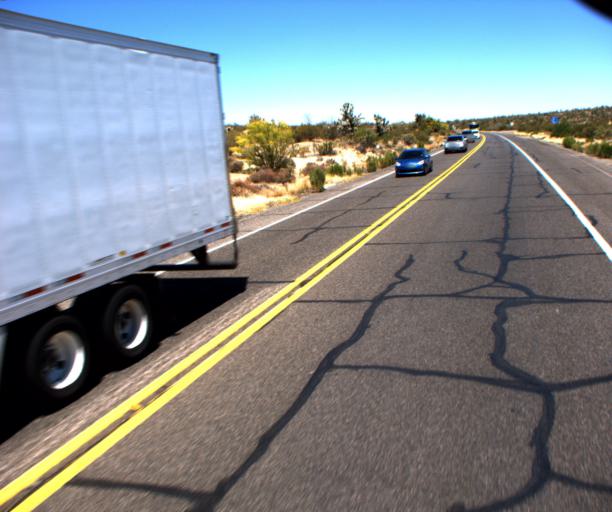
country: US
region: Arizona
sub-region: Yavapai County
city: Congress
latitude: 34.2289
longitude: -113.0700
